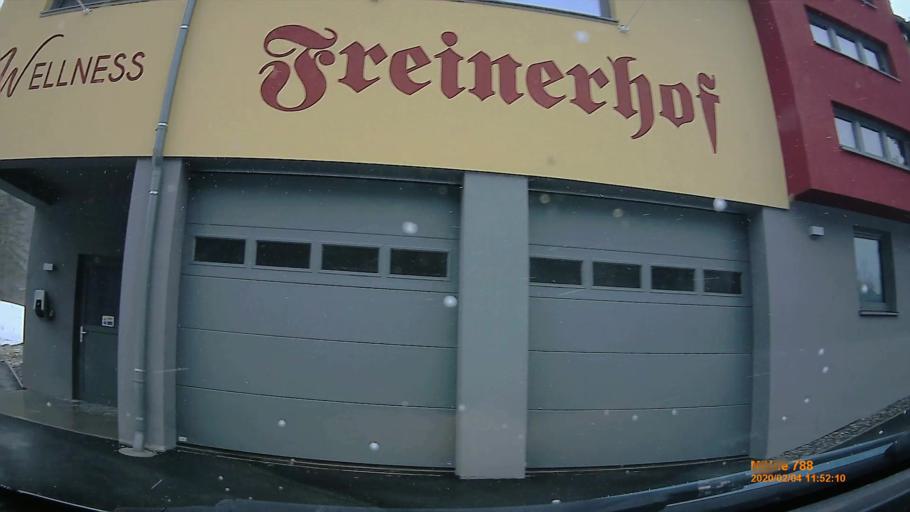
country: AT
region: Styria
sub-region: Politischer Bezirk Bruck-Muerzzuschlag
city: Muerzsteg
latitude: 47.7417
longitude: 15.4849
